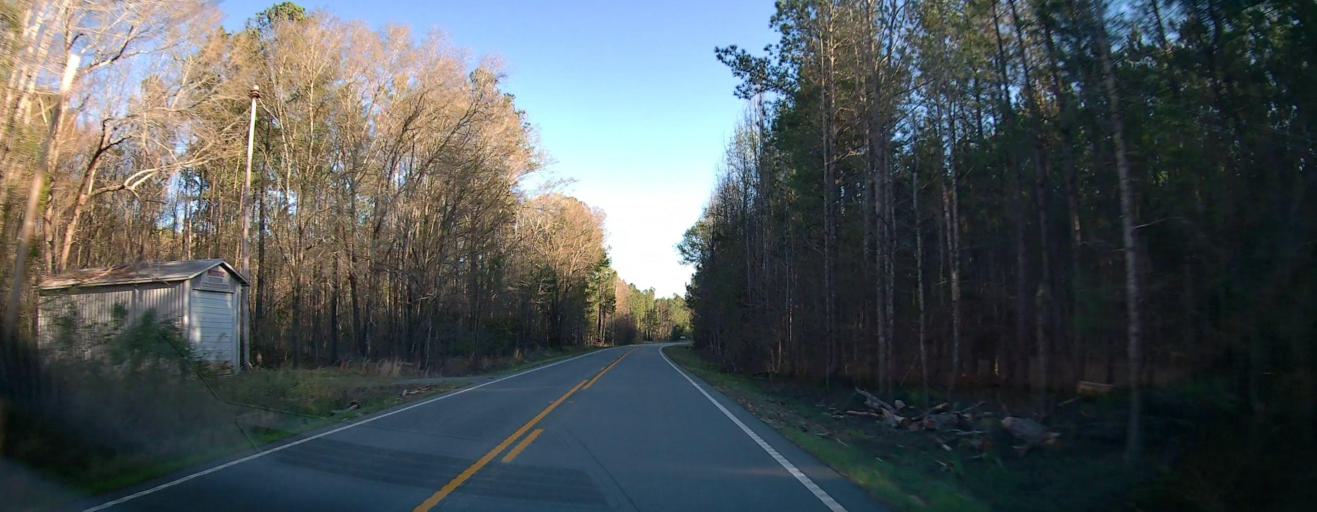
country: US
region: Georgia
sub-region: Pulaski County
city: Hawkinsville
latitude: 32.1984
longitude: -83.3725
